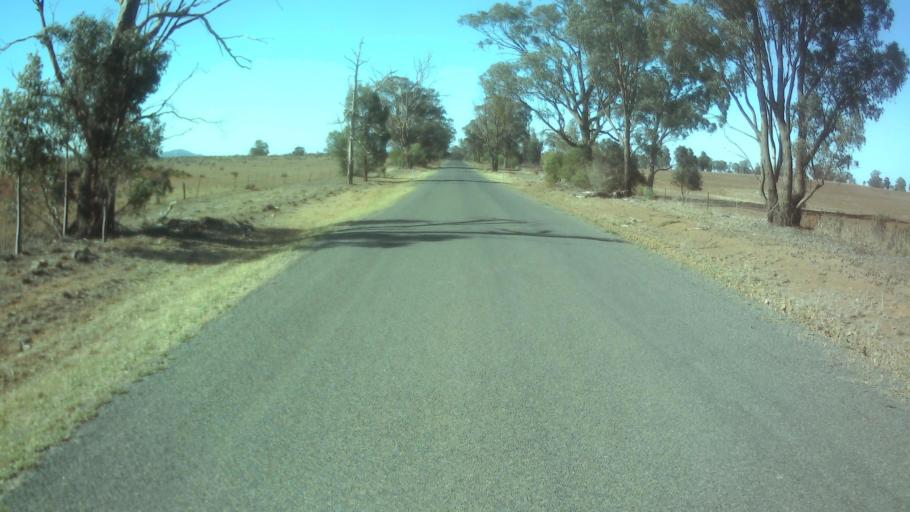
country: AU
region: New South Wales
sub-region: Forbes
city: Forbes
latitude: -33.7010
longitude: 147.8066
